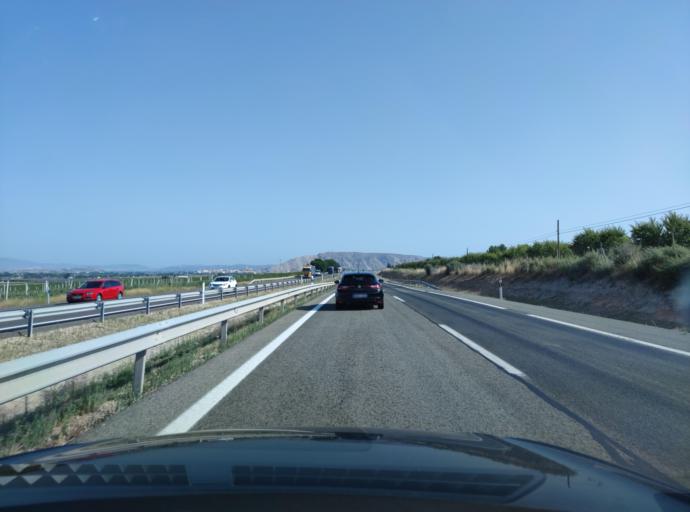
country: ES
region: Valencia
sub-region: Provincia de Alicante
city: Sax
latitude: 38.5851
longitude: -0.8436
